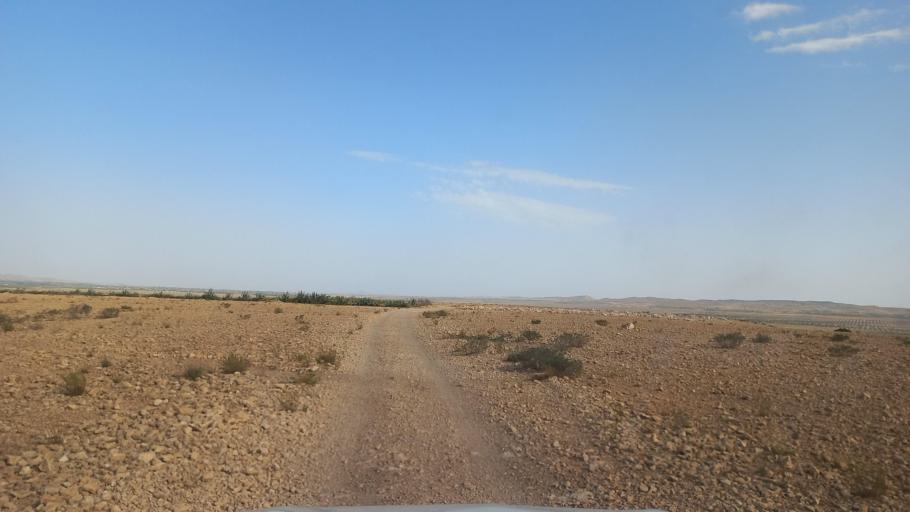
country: TN
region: Al Qasrayn
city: Kasserine
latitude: 35.2588
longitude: 8.9304
